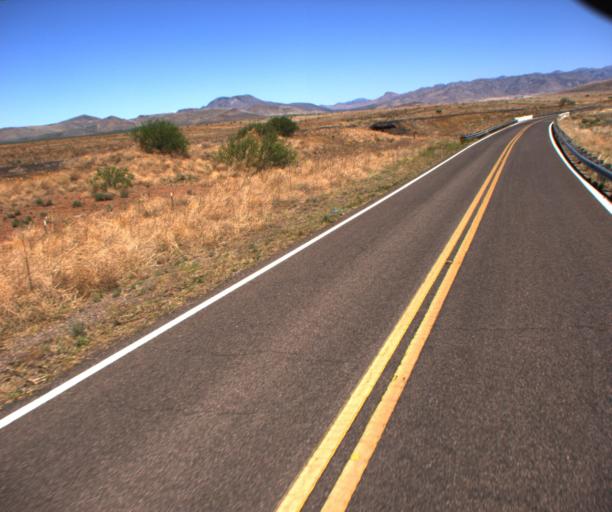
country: US
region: Arizona
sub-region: Cochise County
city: Douglas
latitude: 31.5607
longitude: -109.2654
